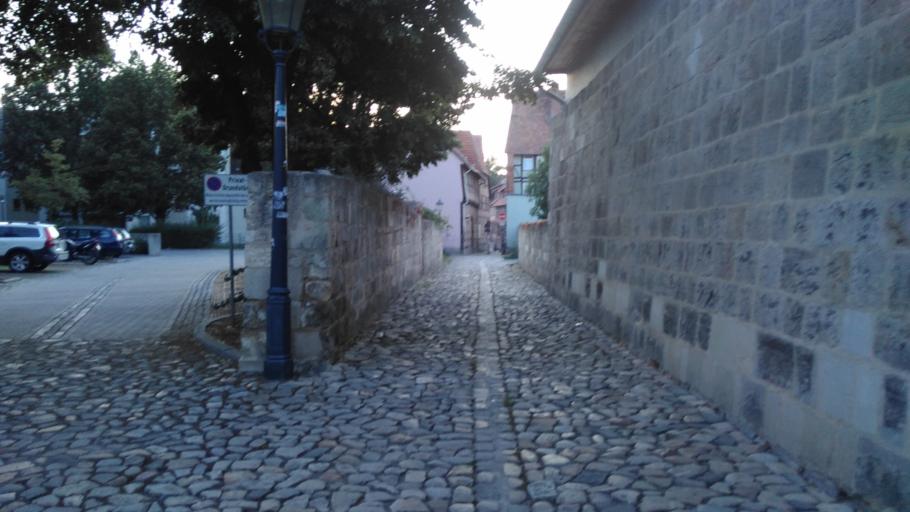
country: DE
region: Saxony-Anhalt
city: Quedlinburg
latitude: 51.7913
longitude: 11.1434
